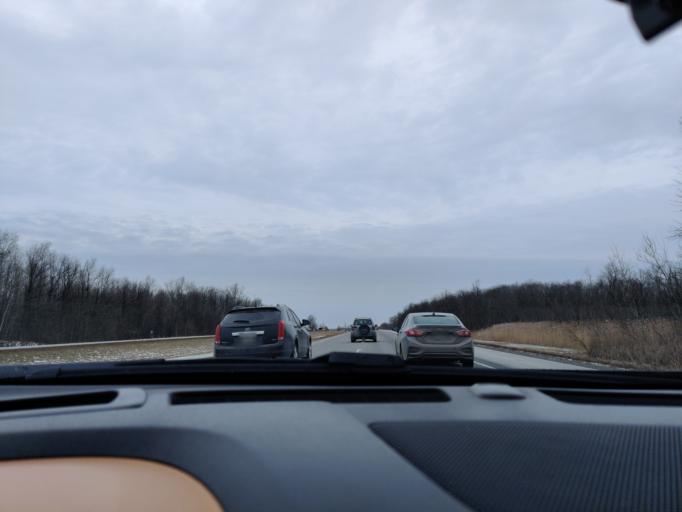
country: US
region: New York
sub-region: St. Lawrence County
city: Norfolk
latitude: 44.9065
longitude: -75.2235
